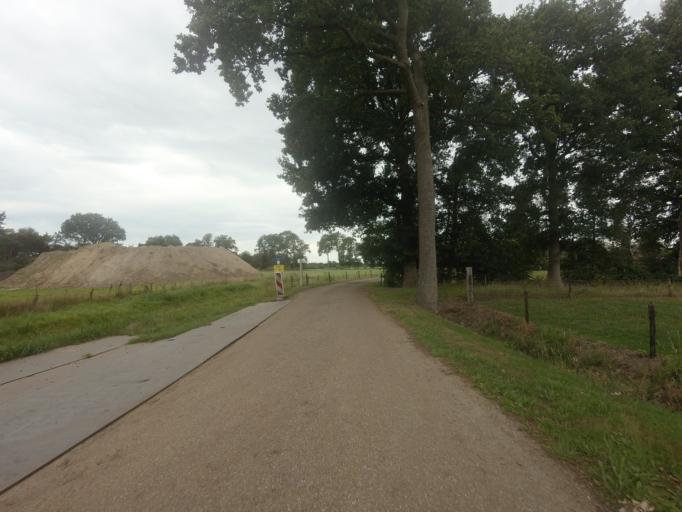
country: NL
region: Overijssel
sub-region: Gemeente Raalte
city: Raalte
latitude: 52.3644
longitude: 6.3404
